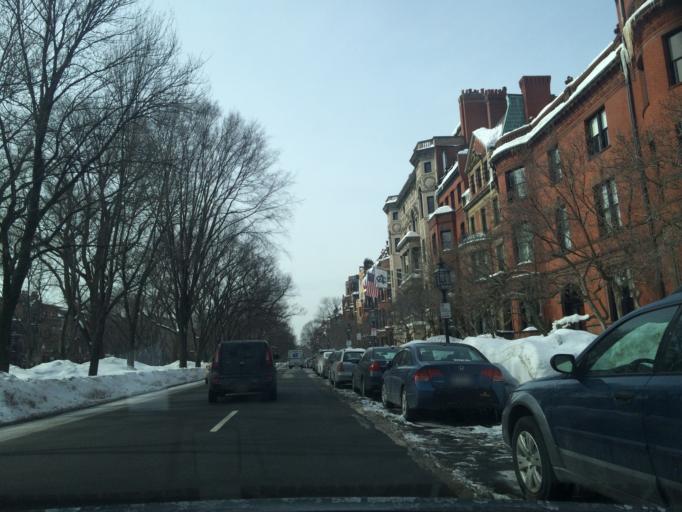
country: US
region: Massachusetts
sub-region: Suffolk County
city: Boston
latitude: 42.3514
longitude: -71.0809
